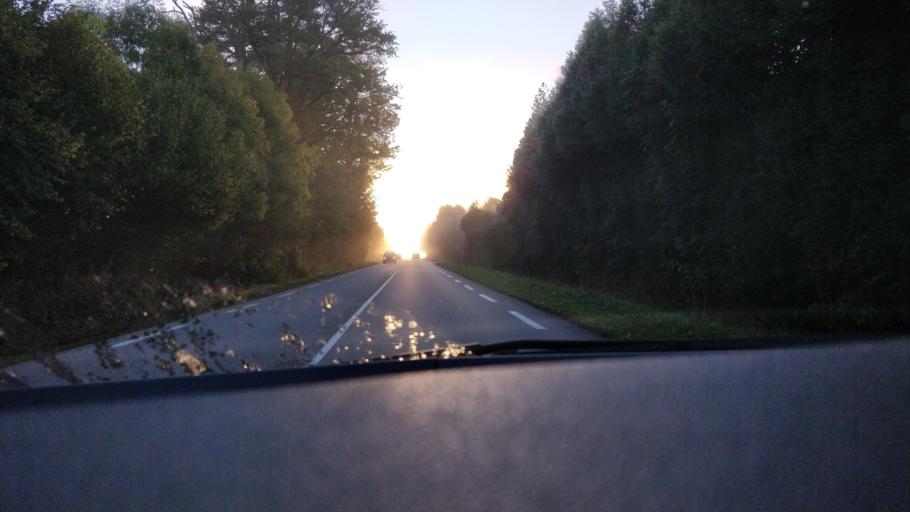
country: FR
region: Limousin
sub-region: Departement de la Haute-Vienne
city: Saint-Just-le-Martel
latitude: 45.8479
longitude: 1.3597
